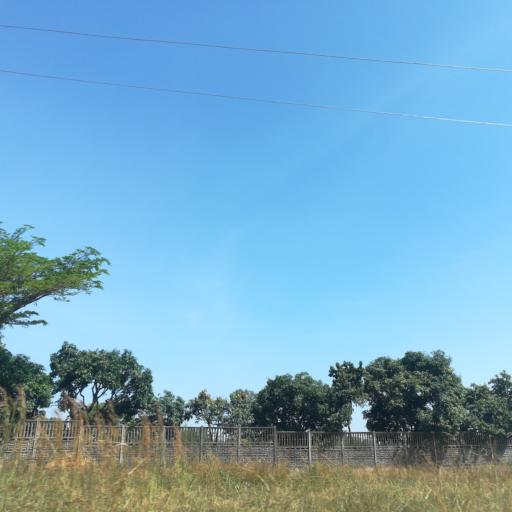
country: NG
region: Plateau
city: Bukuru
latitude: 9.7597
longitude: 8.8626
